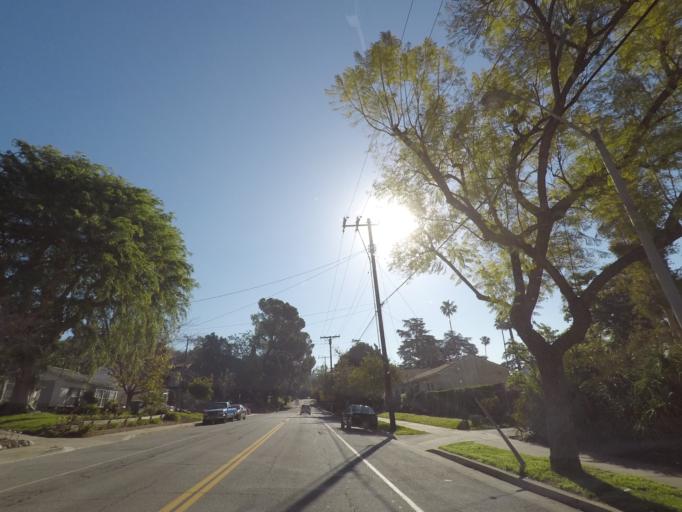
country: US
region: California
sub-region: Los Angeles County
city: North Glendale
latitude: 34.1667
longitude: -118.2521
